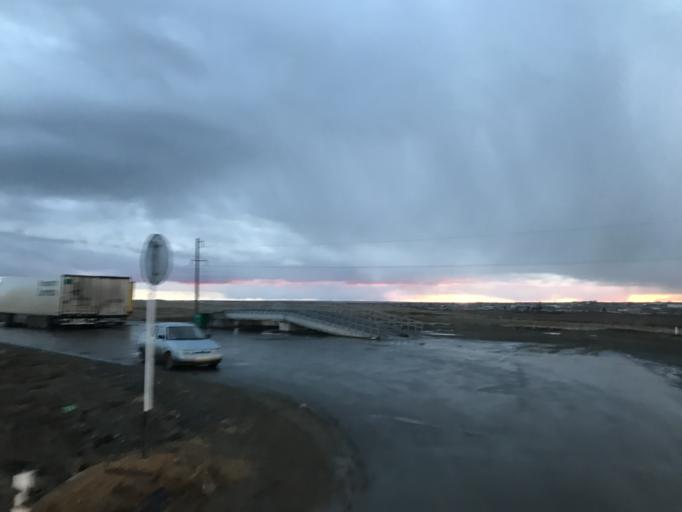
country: KZ
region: Qostanay
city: Ordzhonikidze
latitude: 52.4480
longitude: 61.7720
